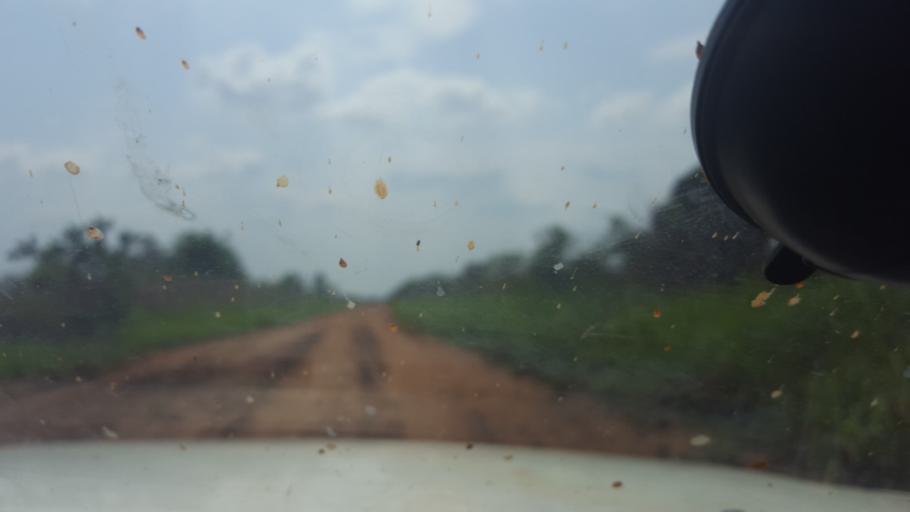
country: CD
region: Bandundu
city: Bandundu
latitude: -3.7617
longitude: 17.1381
